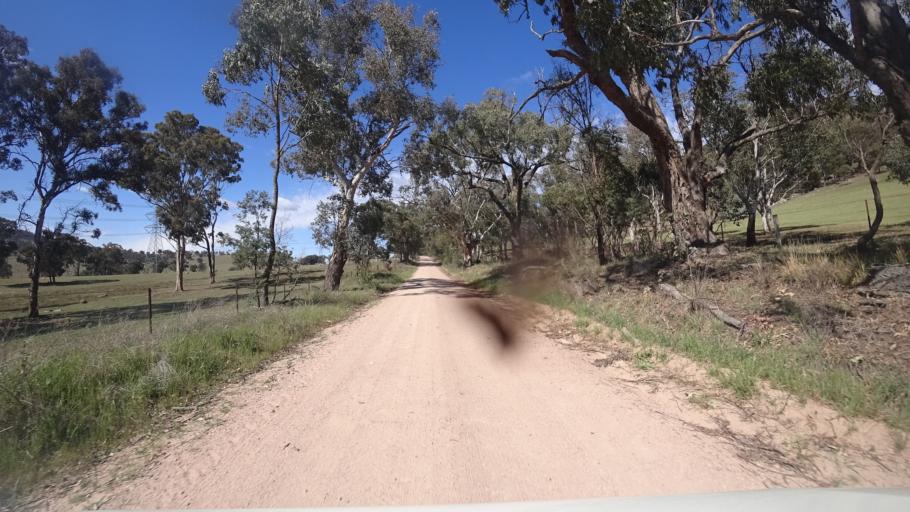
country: AU
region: New South Wales
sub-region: Lithgow
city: Portland
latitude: -33.5293
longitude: 149.9345
